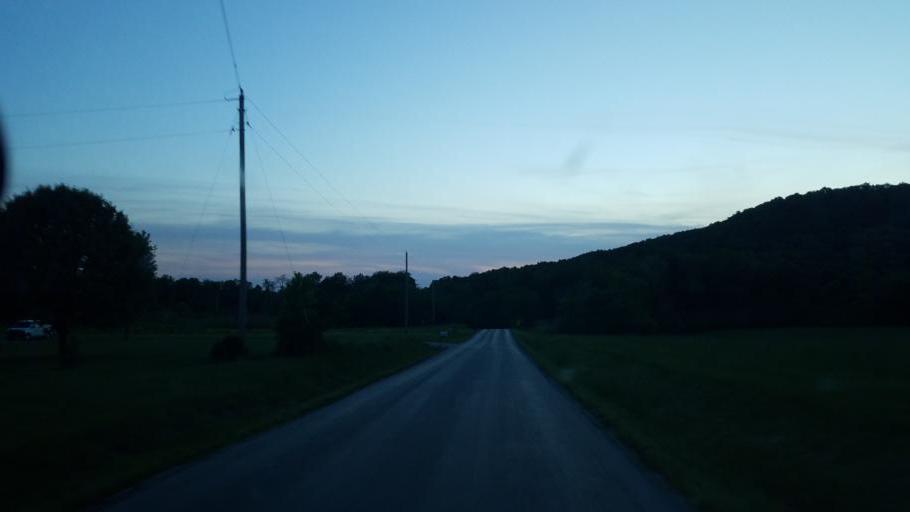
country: US
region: Ohio
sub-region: Highland County
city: Greenfield
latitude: 39.2053
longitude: -83.3645
